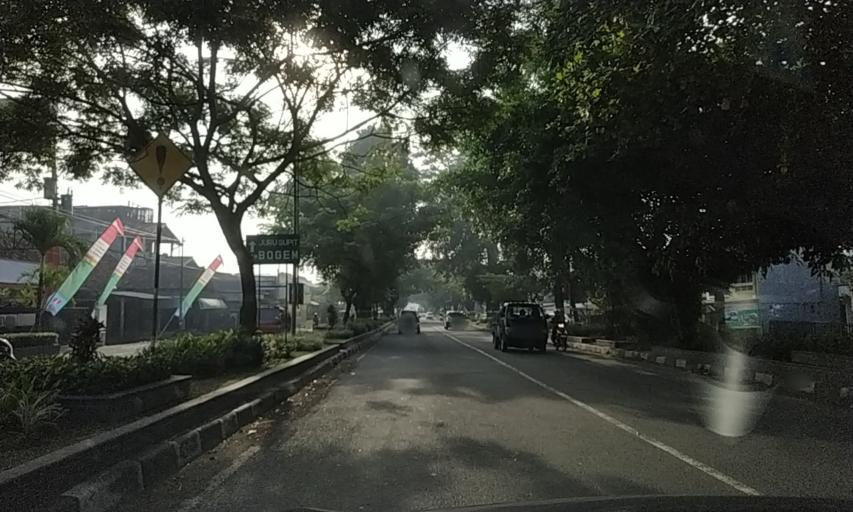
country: ID
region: Central Java
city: Candi Prambanan
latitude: -7.7564
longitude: 110.4839
